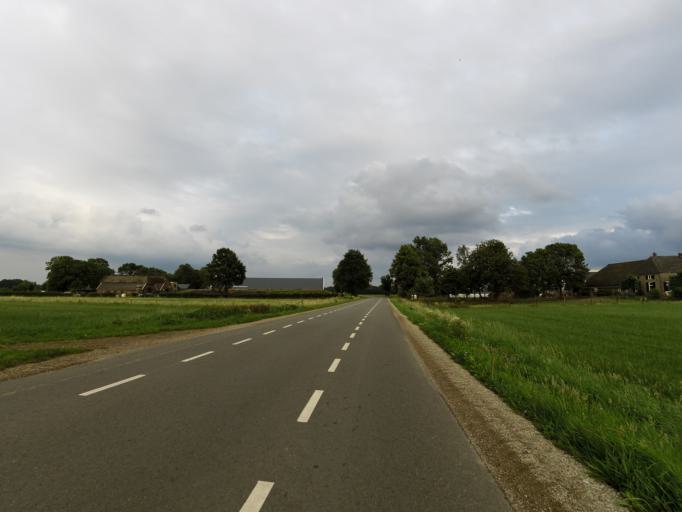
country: NL
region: Gelderland
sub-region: Gemeente Doesburg
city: Doesburg
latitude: 51.9860
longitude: 6.1971
